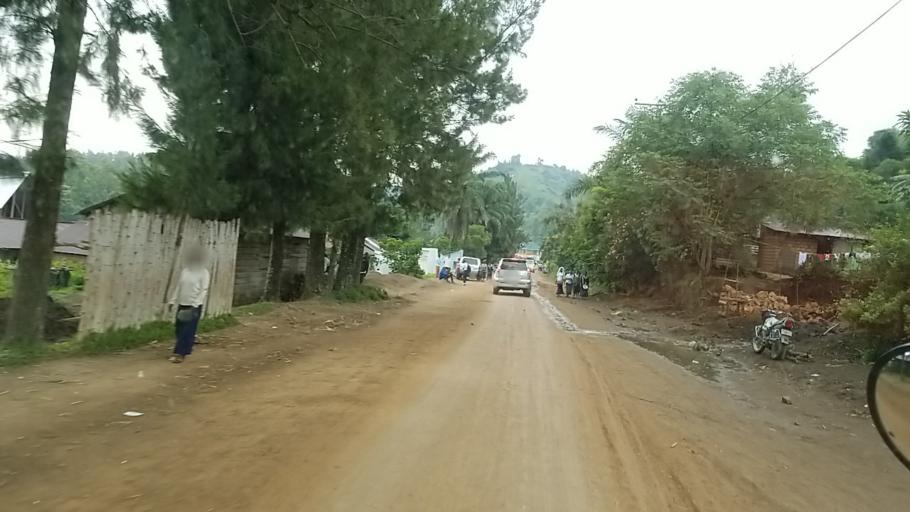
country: CD
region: Nord Kivu
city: Sake
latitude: -1.6967
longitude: 29.0142
